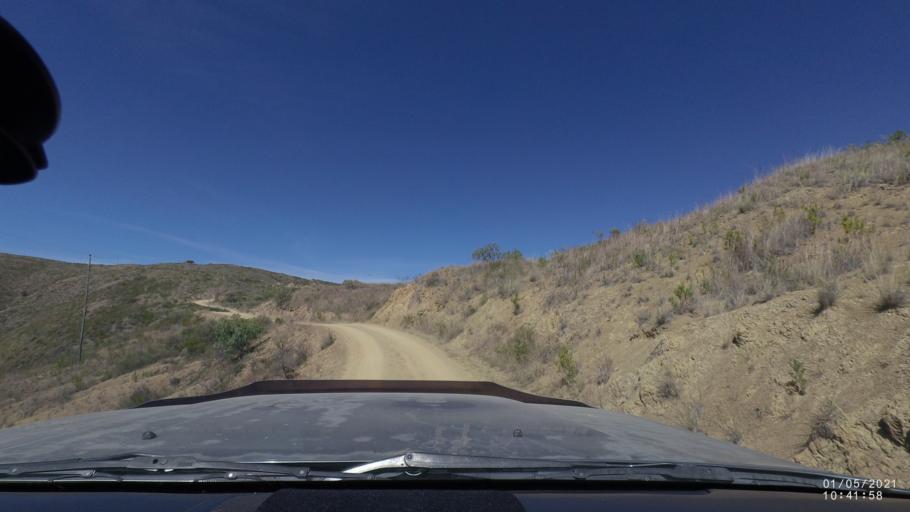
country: BO
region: Cochabamba
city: Capinota
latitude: -17.6105
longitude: -66.1759
